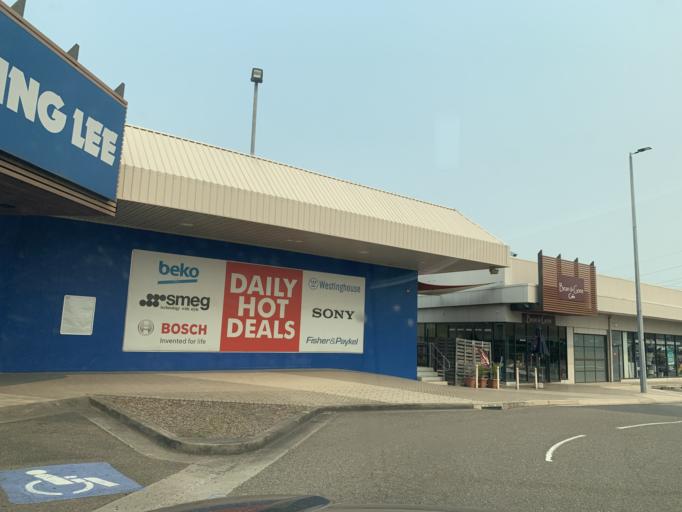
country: AU
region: New South Wales
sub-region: Holroyd
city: Girraween
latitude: -33.8006
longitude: 150.9198
